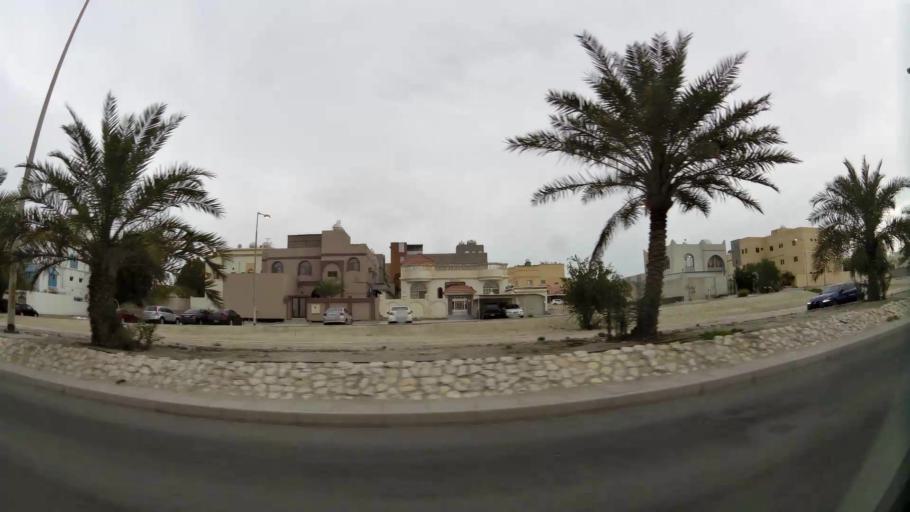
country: BH
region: Central Governorate
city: Madinat Hamad
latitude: 26.1004
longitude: 50.4992
